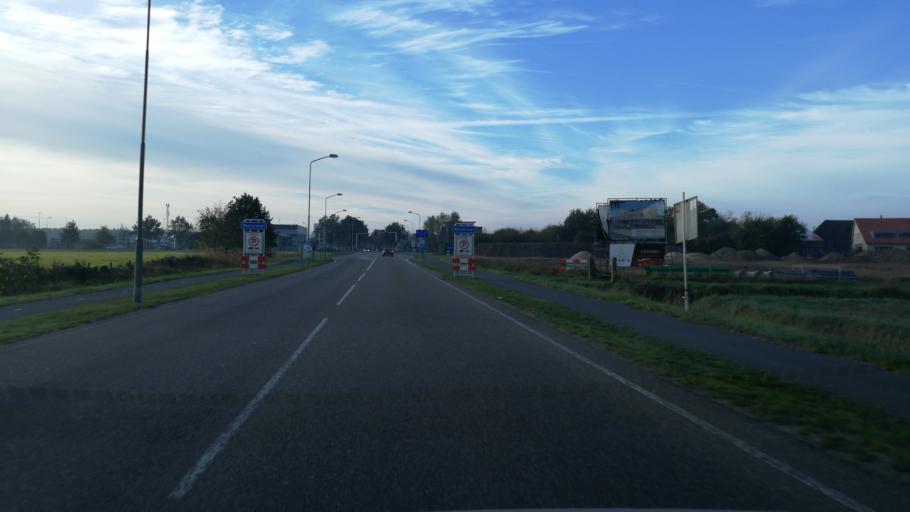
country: NL
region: Gelderland
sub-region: Gemeente Westervoort
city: Westervoort
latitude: 51.9626
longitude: 5.9838
